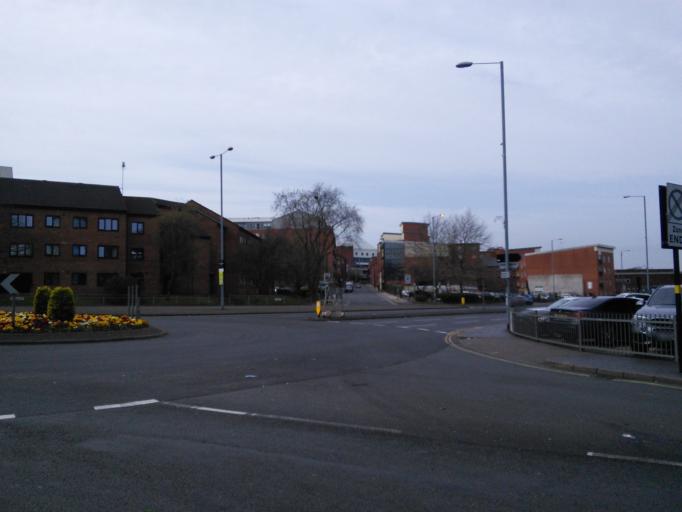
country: GB
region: England
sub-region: City and Borough of Birmingham
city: Birmingham
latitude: 52.4824
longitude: -1.9108
